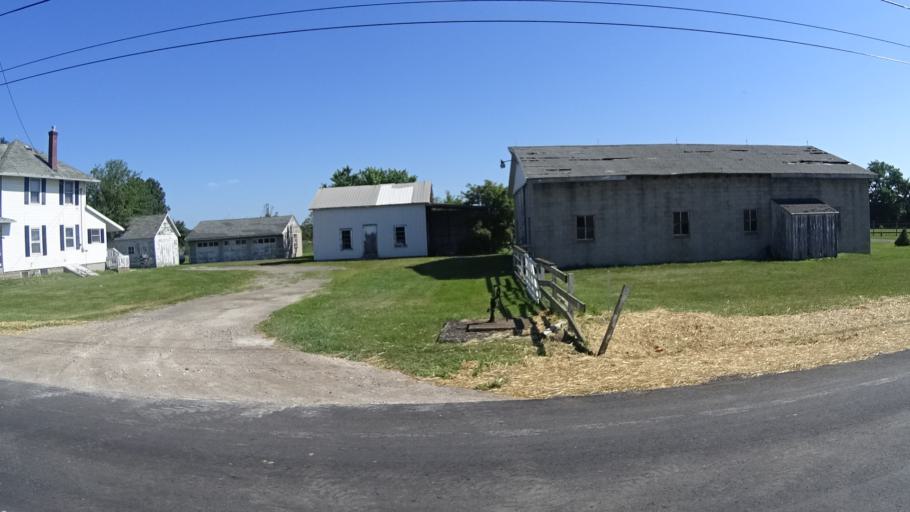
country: US
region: Ohio
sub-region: Erie County
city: Huron
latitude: 41.3914
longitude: -82.6229
